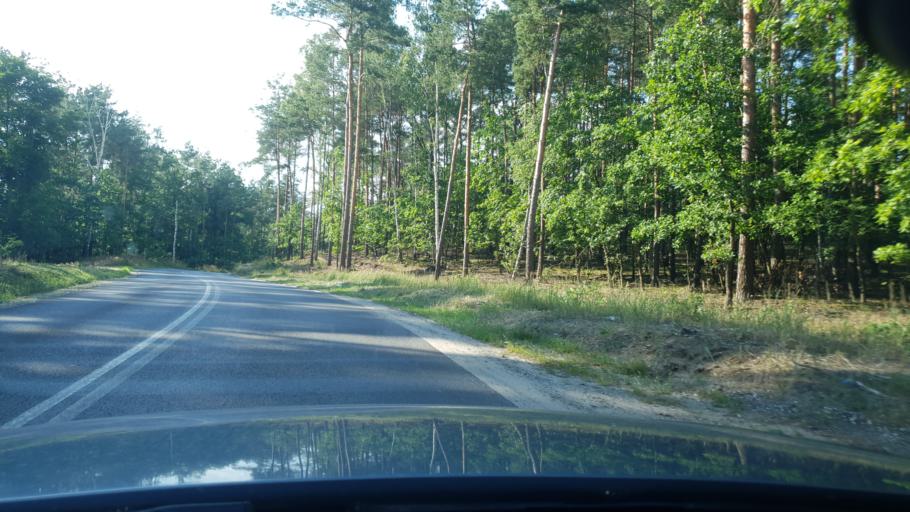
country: PL
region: Kujawsko-Pomorskie
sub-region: Grudziadz
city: Grudziadz
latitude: 53.4424
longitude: 18.7551
